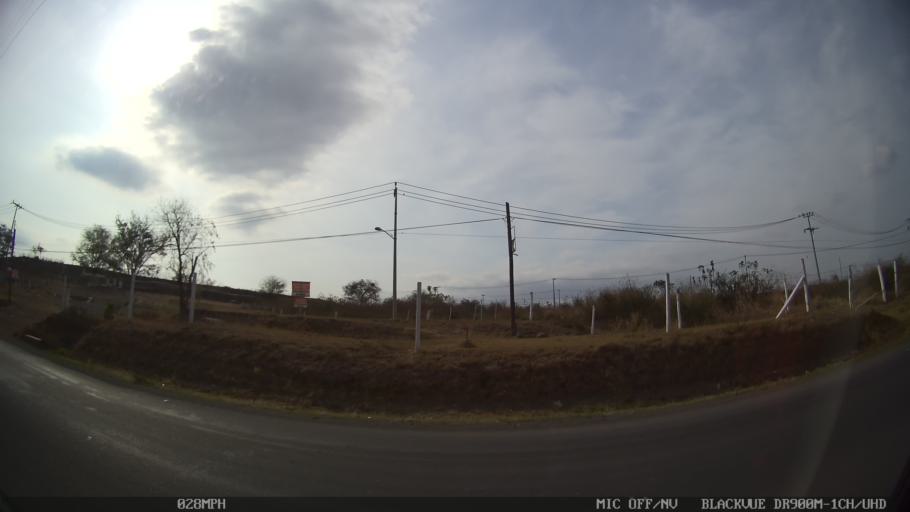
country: MX
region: Jalisco
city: Tonala
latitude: 20.6201
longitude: -103.2227
